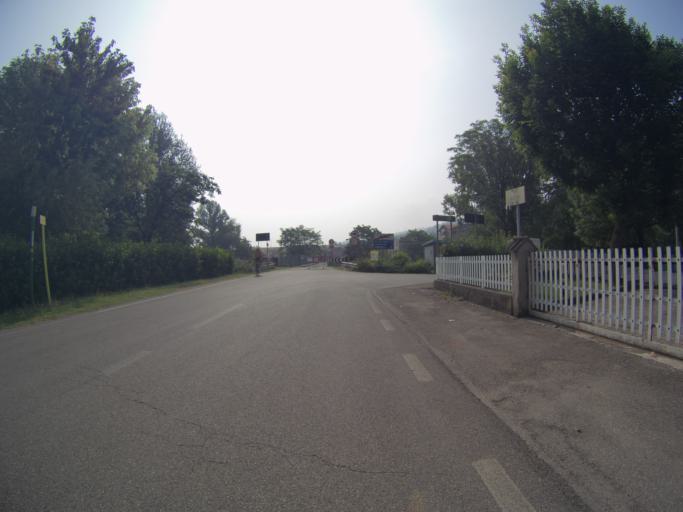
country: IT
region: Emilia-Romagna
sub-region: Provincia di Reggio Emilia
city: Pratissolo
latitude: 44.5884
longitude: 10.6712
